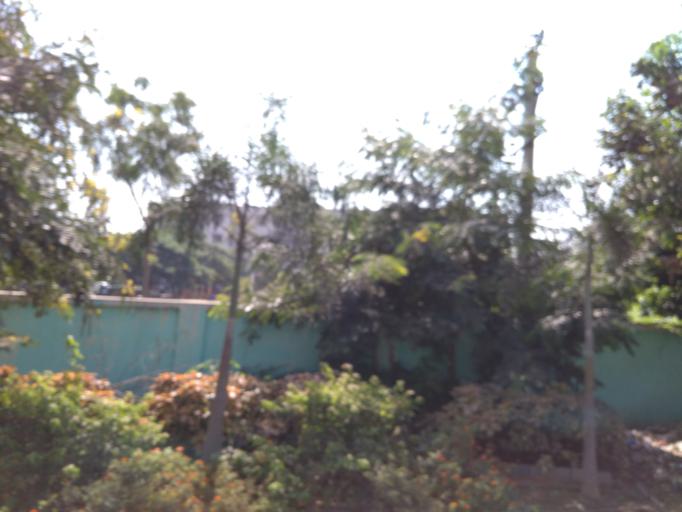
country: IN
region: Andhra Pradesh
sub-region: Krishna
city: Gannavaram
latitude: 16.5114
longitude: 80.7417
